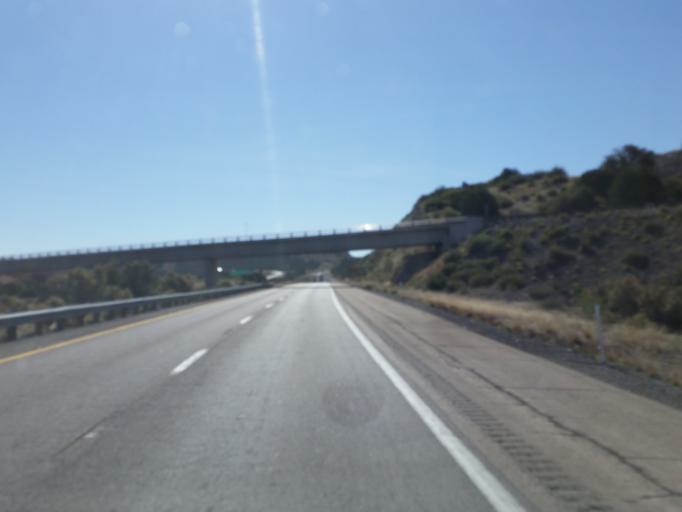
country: US
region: Arizona
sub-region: Mohave County
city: Peach Springs
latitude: 35.1904
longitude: -113.4362
